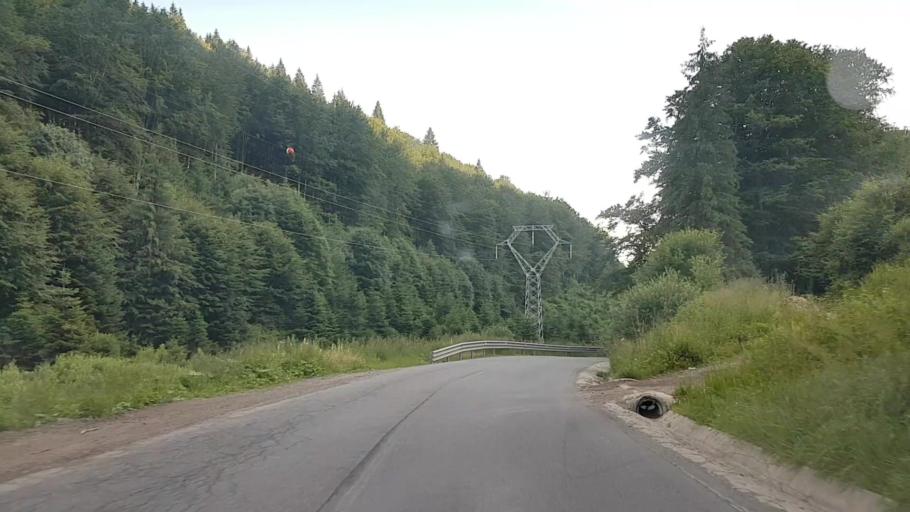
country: RO
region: Harghita
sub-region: Comuna Praid
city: Ocna de Sus
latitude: 46.6199
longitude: 25.2506
